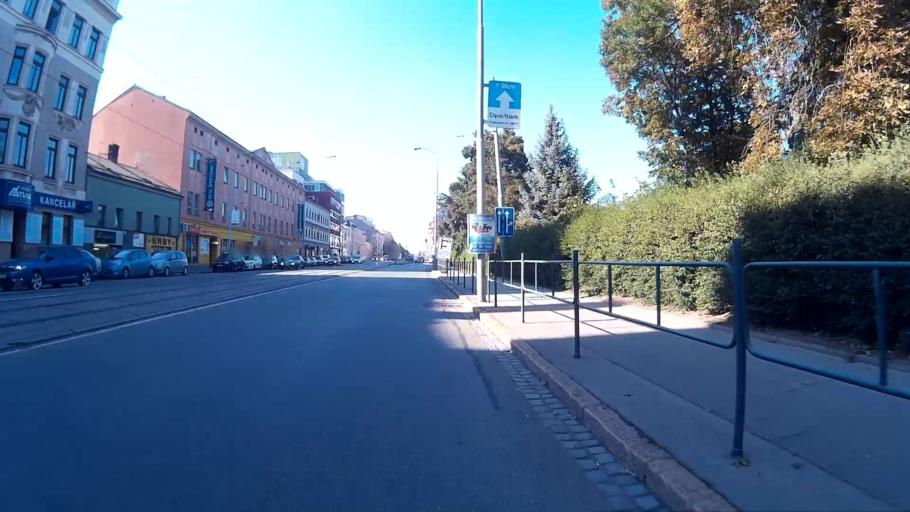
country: CZ
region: South Moravian
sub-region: Mesto Brno
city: Brno
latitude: 49.2064
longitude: 16.6053
